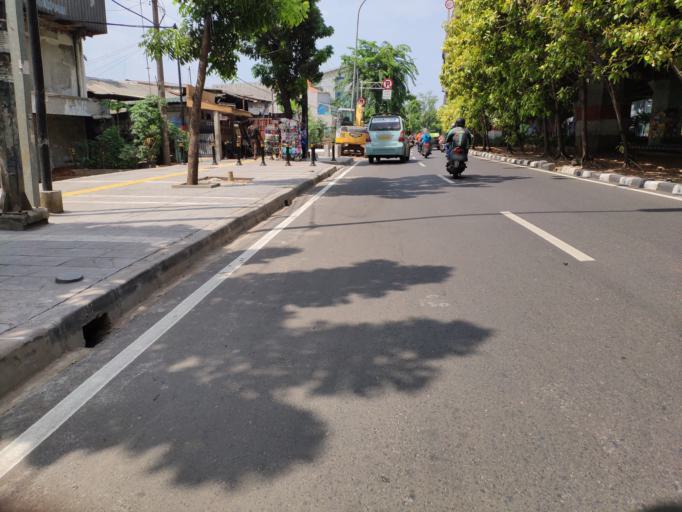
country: ID
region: Jakarta Raya
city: Jakarta
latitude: -6.2033
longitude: 106.8731
